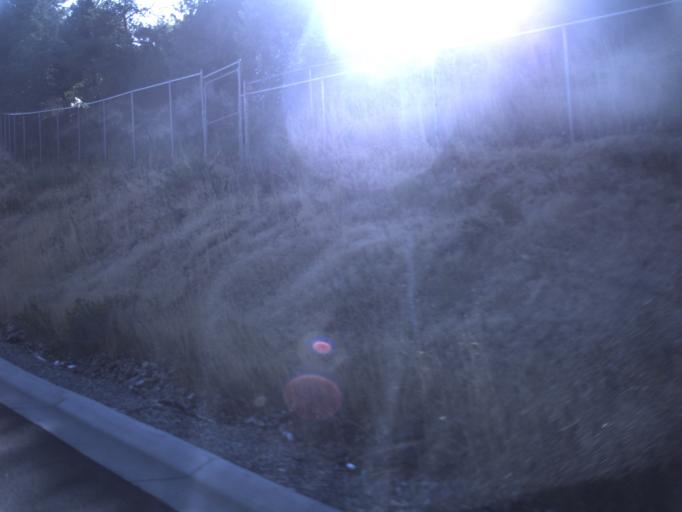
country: US
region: Utah
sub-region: Salt Lake County
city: Cottonwood Heights
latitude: 40.6142
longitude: -111.7890
